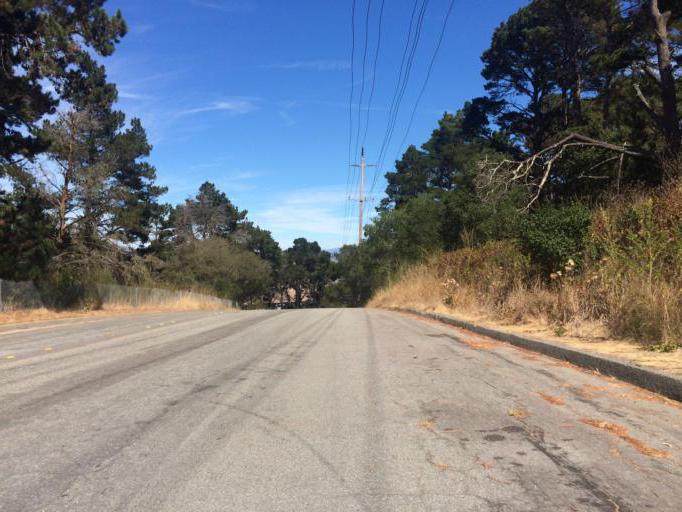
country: US
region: California
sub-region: Monterey County
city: Monterey
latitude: 36.5806
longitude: -121.9018
